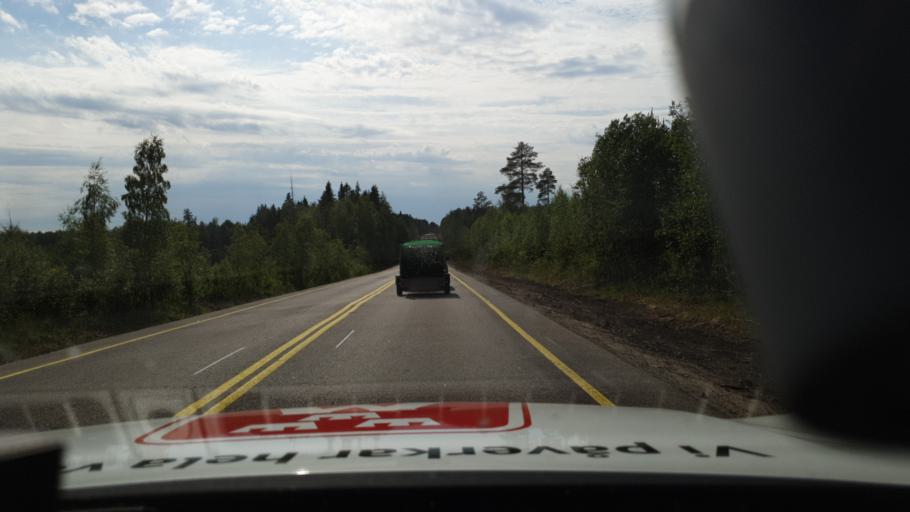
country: SE
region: Norrbotten
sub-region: Lulea Kommun
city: Ranea
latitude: 65.8675
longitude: 22.3233
